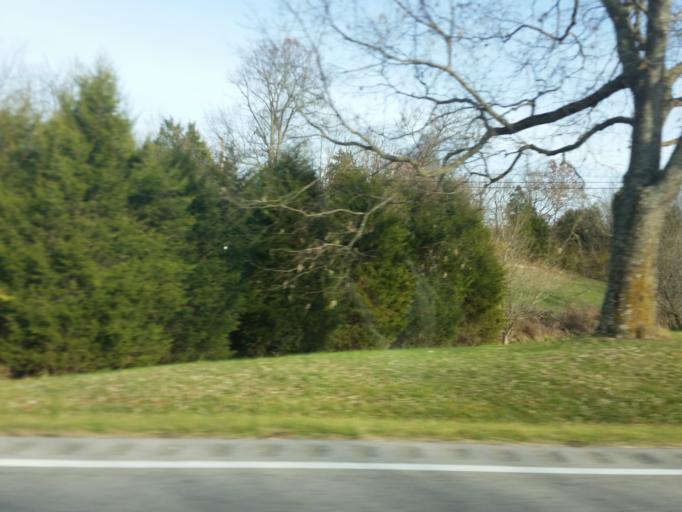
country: US
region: Kentucky
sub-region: Harrison County
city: Cynthiana
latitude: 38.4484
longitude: -84.2831
